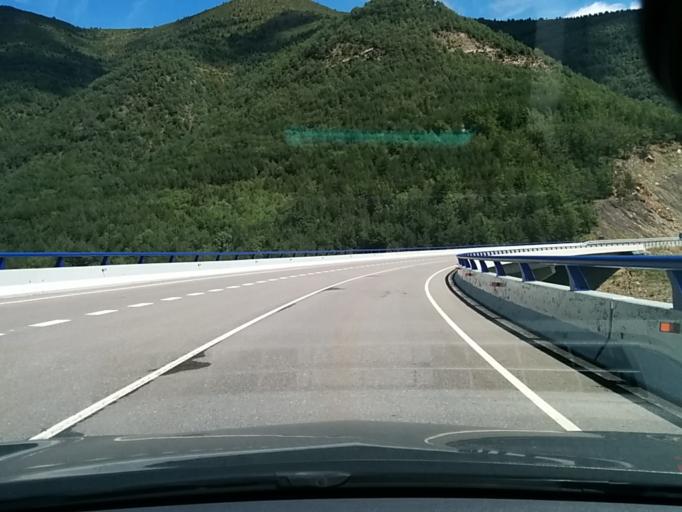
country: ES
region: Aragon
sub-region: Provincia de Huesca
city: Fiscal
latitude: 42.4987
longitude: -0.1537
